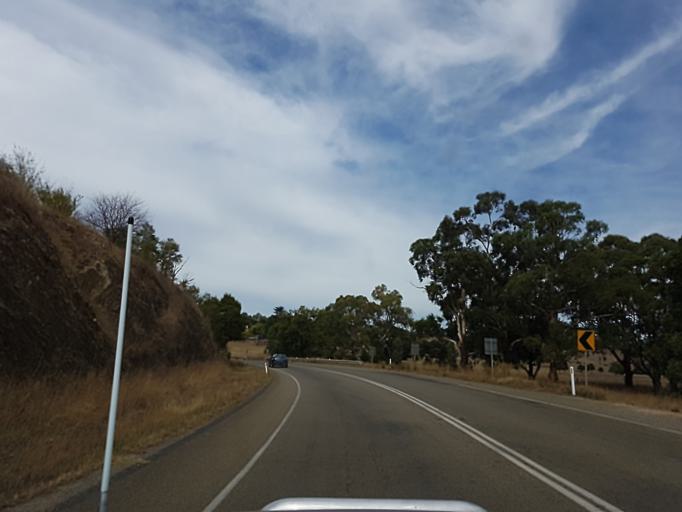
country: AU
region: Victoria
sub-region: Murrindindi
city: Alexandra
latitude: -37.2122
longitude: 145.4388
